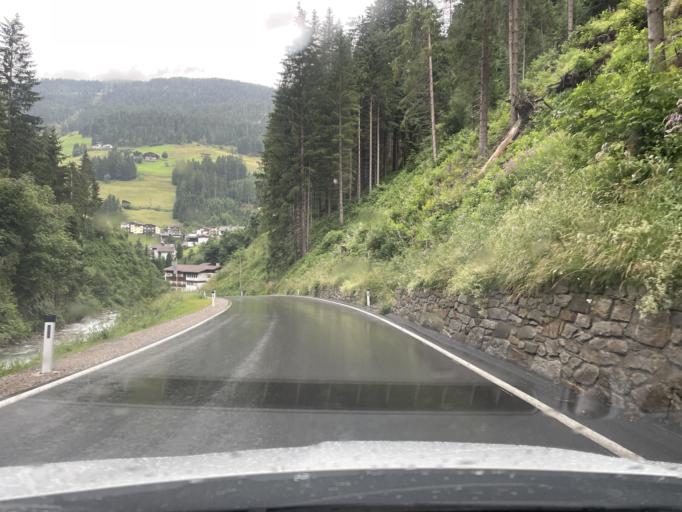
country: AT
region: Tyrol
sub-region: Politischer Bezirk Lienz
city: Ausservillgraten
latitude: 46.7887
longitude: 12.4345
